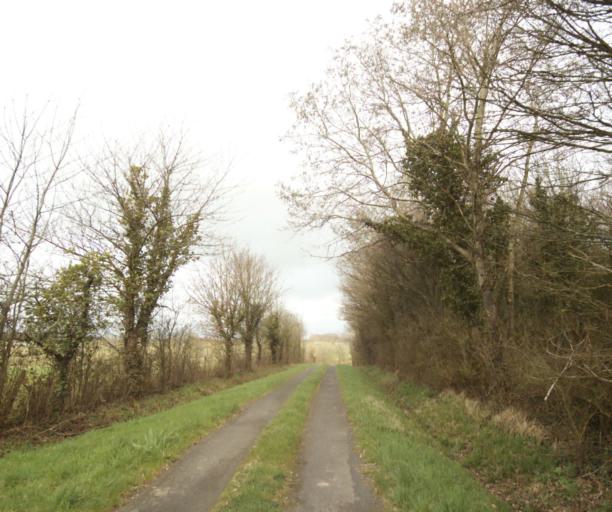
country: FR
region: Pays de la Loire
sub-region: Departement de la Loire-Atlantique
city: Bouvron
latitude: 47.4283
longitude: -1.8921
